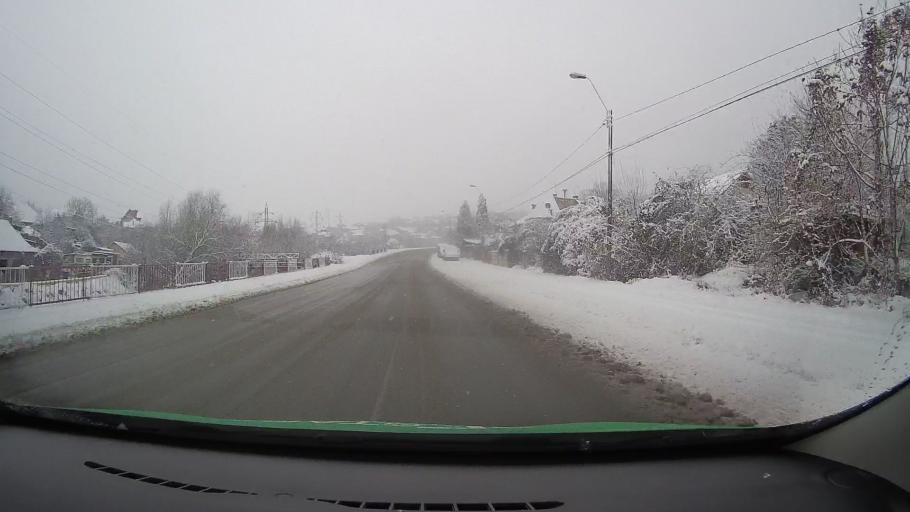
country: RO
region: Hunedoara
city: Hunedoara
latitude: 45.7487
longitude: 22.8927
